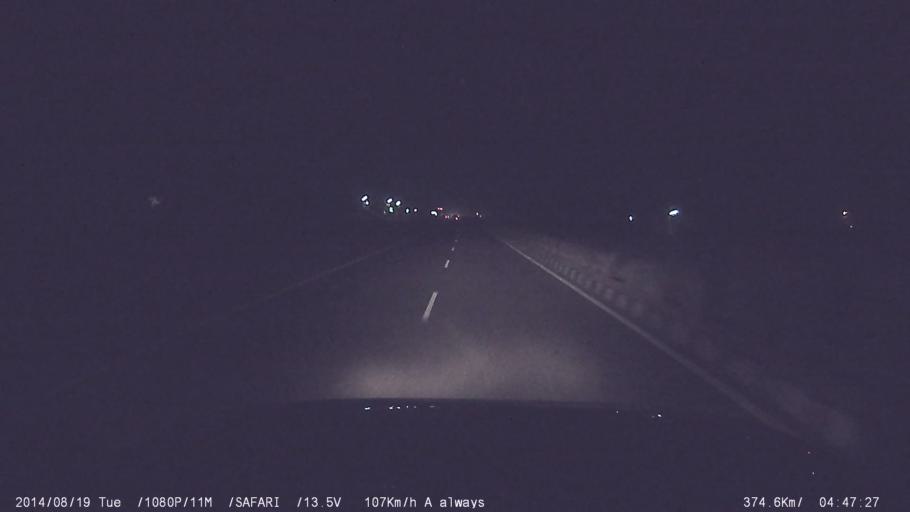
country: IN
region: Tamil Nadu
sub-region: Erode
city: Bhavani
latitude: 11.4464
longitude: 77.7369
